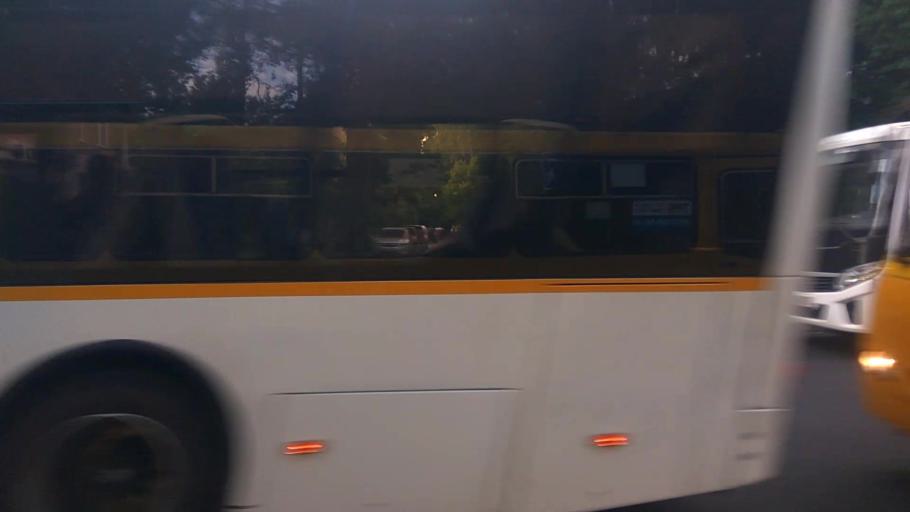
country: RU
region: Moskovskaya
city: Mytishchi
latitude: 55.9111
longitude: 37.7374
